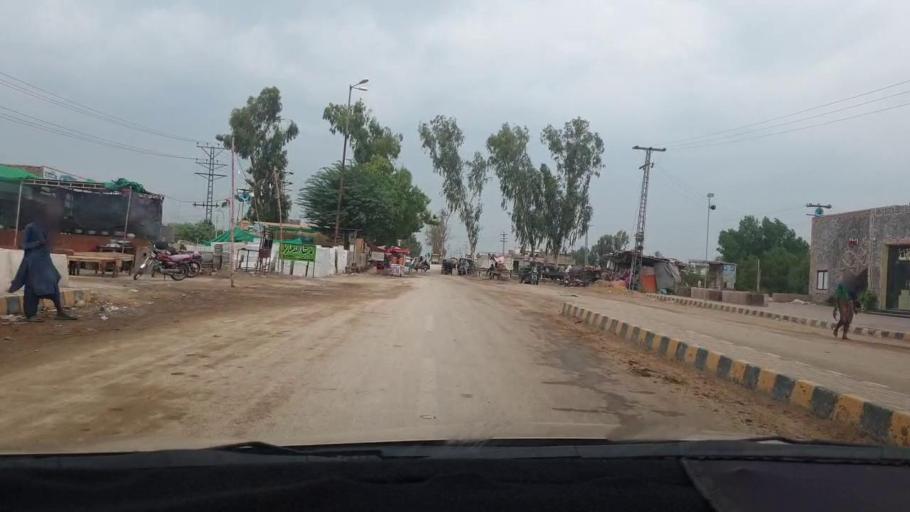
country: PK
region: Sindh
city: Larkana
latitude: 27.5777
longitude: 68.2247
